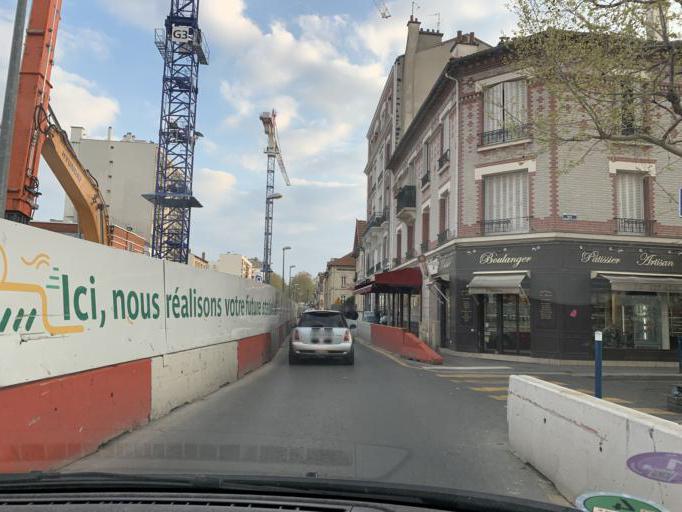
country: FR
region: Ile-de-France
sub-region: Departement de Seine-Saint-Denis
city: Aubervilliers
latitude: 48.9137
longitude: 2.3806
